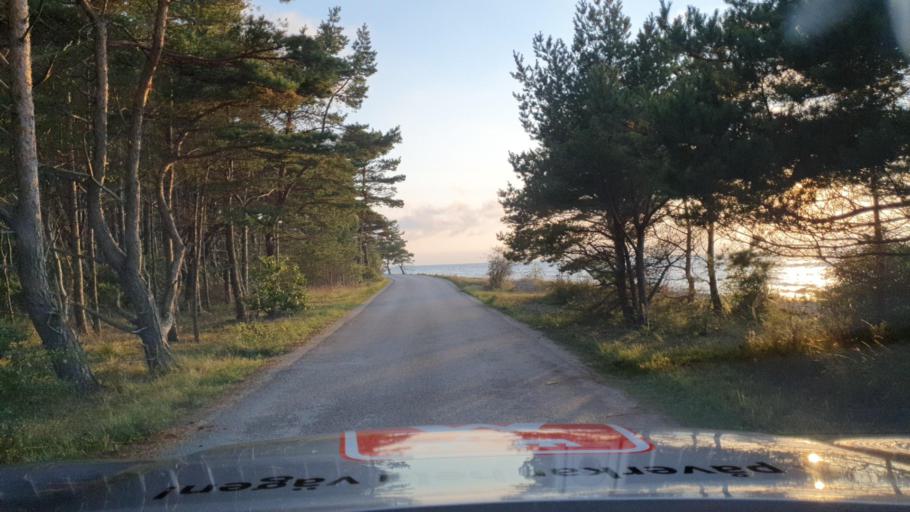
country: SE
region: Gotland
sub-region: Gotland
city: Klintehamn
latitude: 57.2924
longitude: 18.1113
